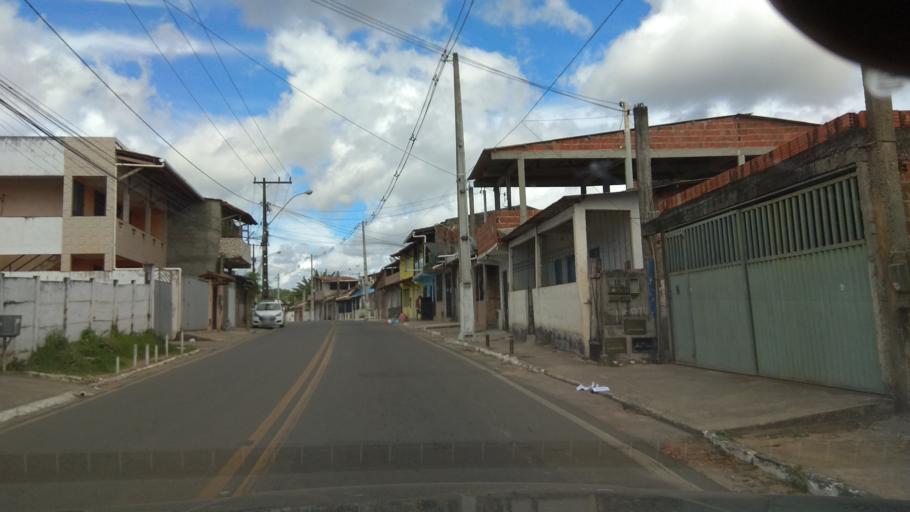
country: BR
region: Bahia
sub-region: Ilheus
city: Ilheus
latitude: -14.7848
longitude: -39.0596
